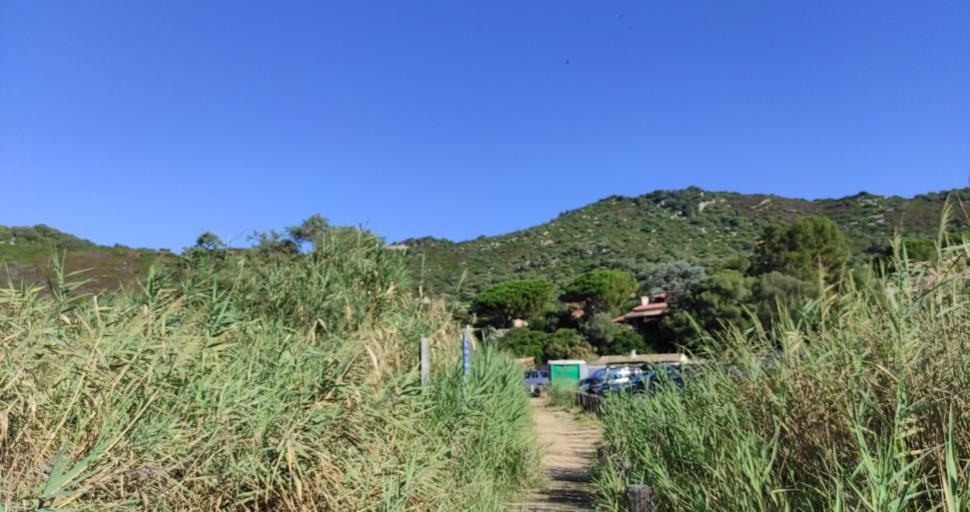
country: FR
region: Corsica
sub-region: Departement de la Corse-du-Sud
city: Alata
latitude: 41.9931
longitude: 8.6687
